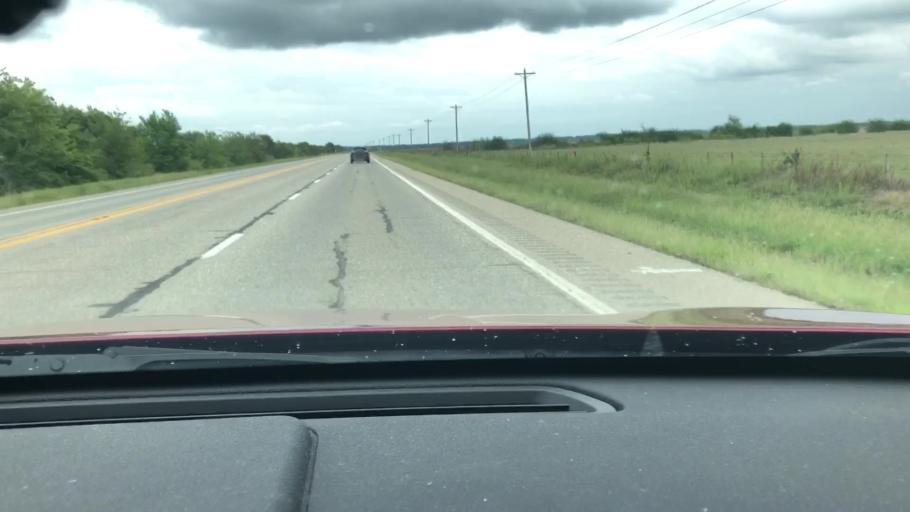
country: US
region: Arkansas
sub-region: Lafayette County
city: Lewisville
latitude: 33.4124
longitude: -93.7894
